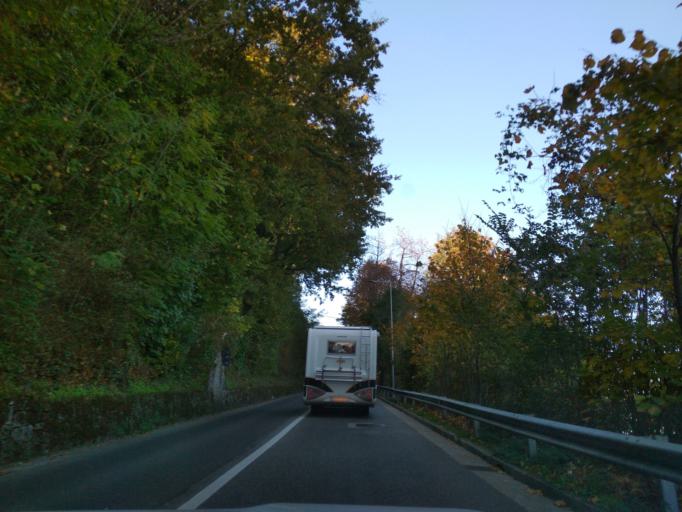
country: SM
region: San Marino
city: San Marino
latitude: 43.9393
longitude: 12.4451
